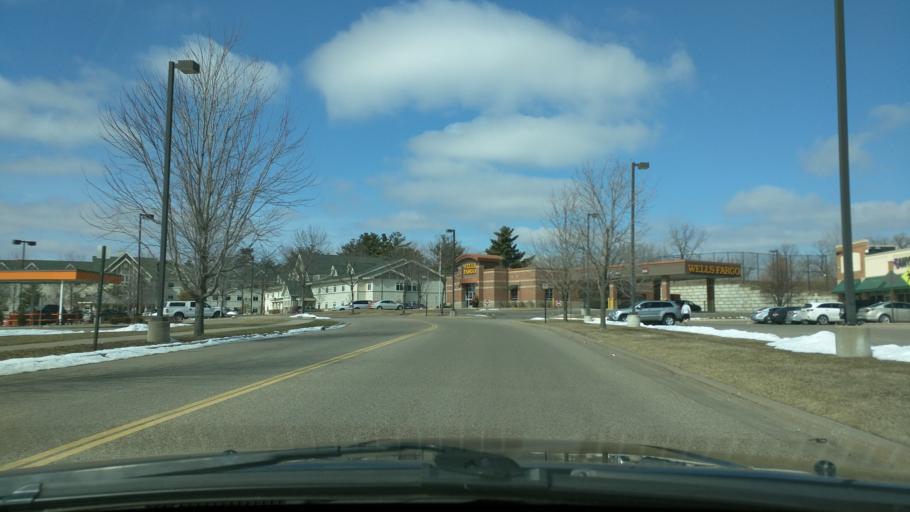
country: US
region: Minnesota
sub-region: Dakota County
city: Inver Grove Heights
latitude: 44.8184
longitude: -93.0420
